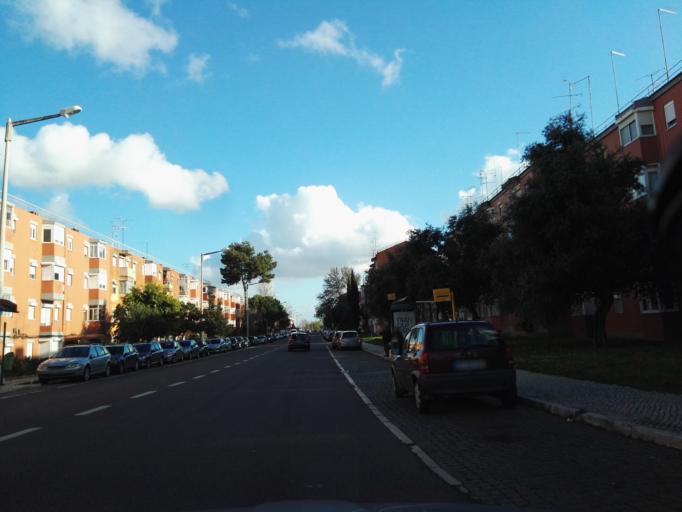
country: PT
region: Lisbon
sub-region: Loures
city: Moscavide
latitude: 38.7745
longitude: -9.1114
